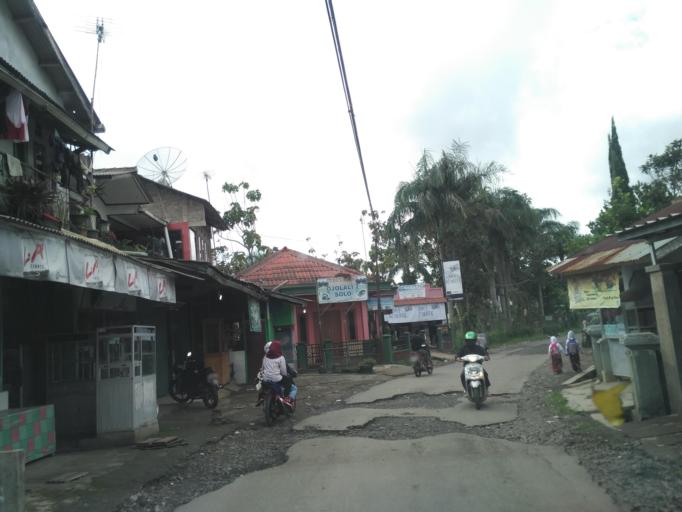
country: ID
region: West Java
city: Ciranjang-hilir
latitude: -6.7322
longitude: 107.0861
